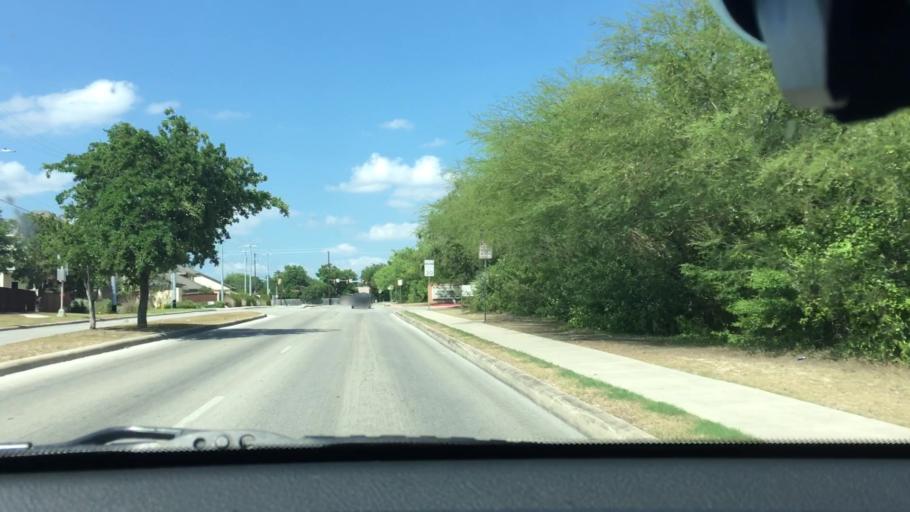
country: US
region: Texas
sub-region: Bexar County
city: Live Oak
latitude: 29.5966
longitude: -98.3865
